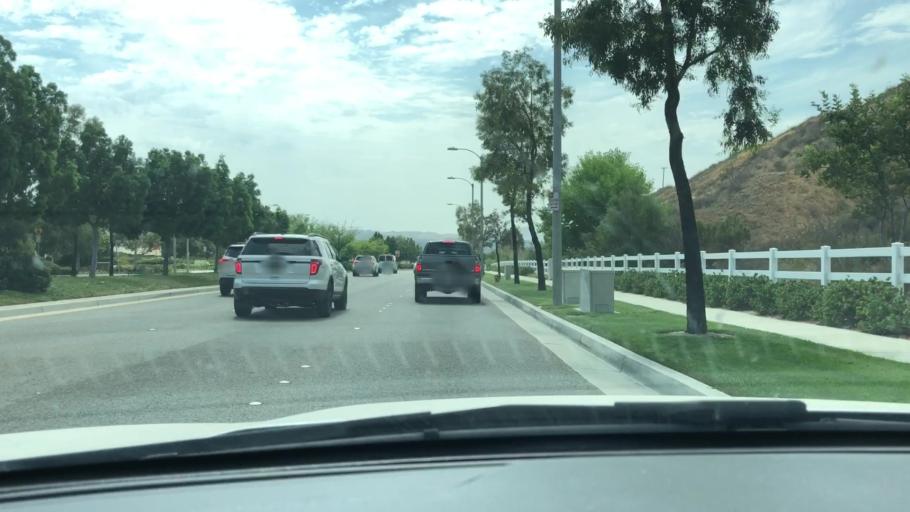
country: US
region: California
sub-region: Los Angeles County
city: Santa Clarita
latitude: 34.4250
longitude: -118.5245
